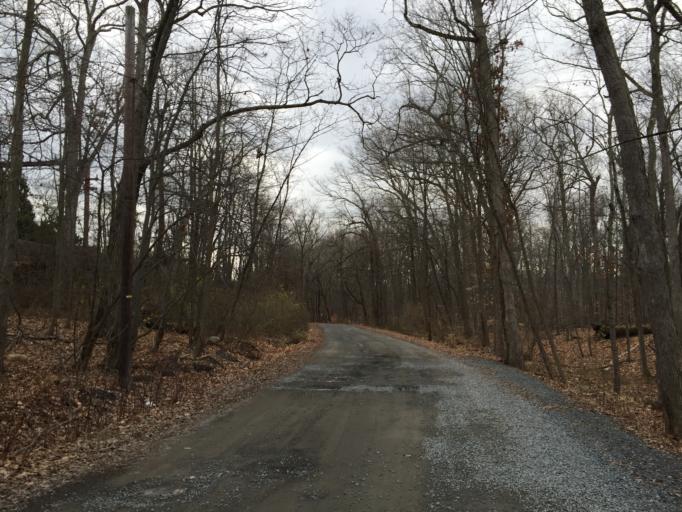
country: US
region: New Jersey
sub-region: Morris County
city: Chatham
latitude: 40.7214
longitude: -74.3899
